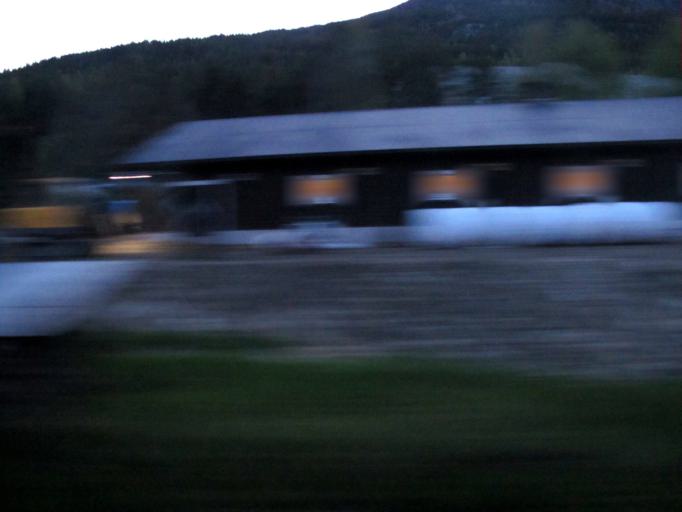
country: NO
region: Oppland
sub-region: Sel
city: Otta
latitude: 61.6592
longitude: 9.6107
